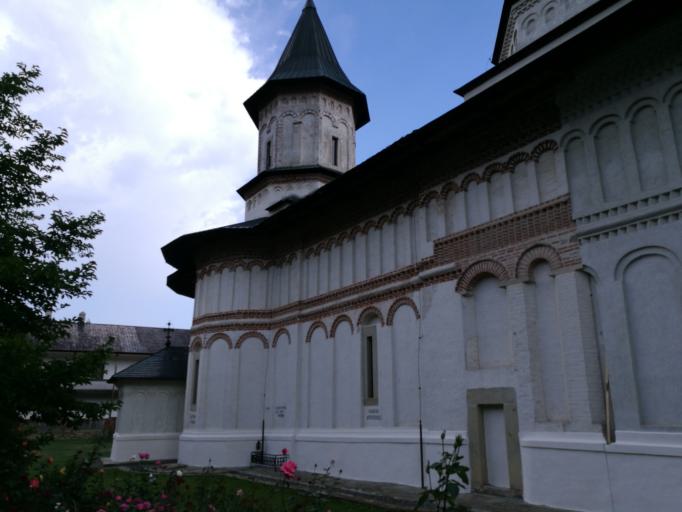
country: RO
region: Neamt
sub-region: Comuna Pipirig
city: Stanca
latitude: 47.2004
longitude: 26.1845
